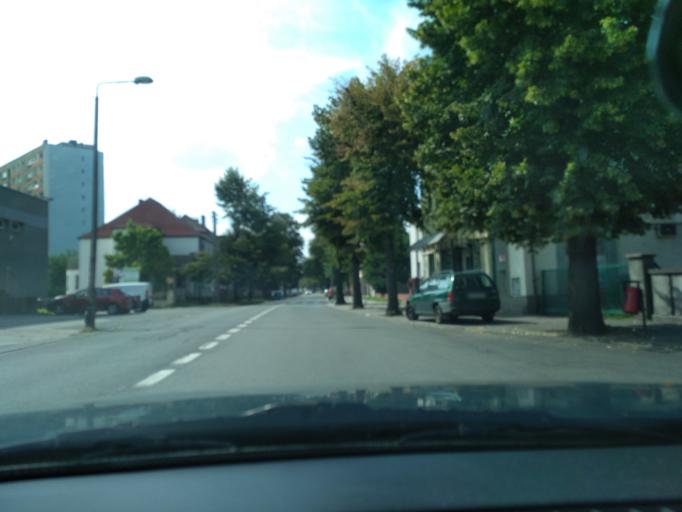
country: PL
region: Silesian Voivodeship
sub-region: Powiat raciborski
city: Raciborz
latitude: 50.0821
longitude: 18.2057
